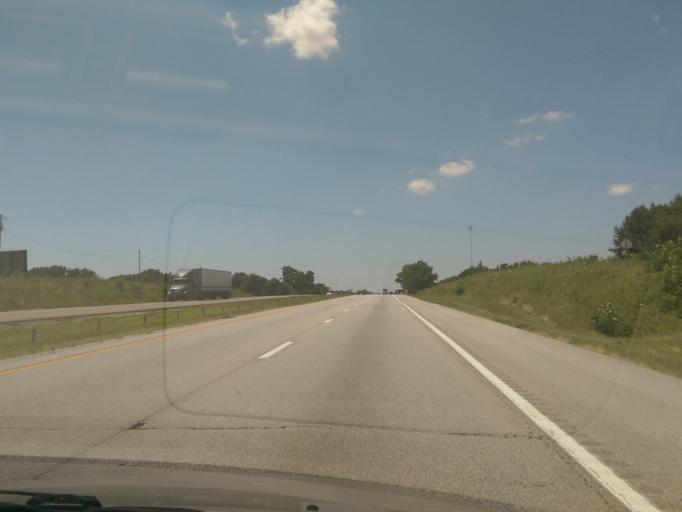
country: US
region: Missouri
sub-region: Cooper County
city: Boonville
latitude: 38.9353
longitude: -92.8160
